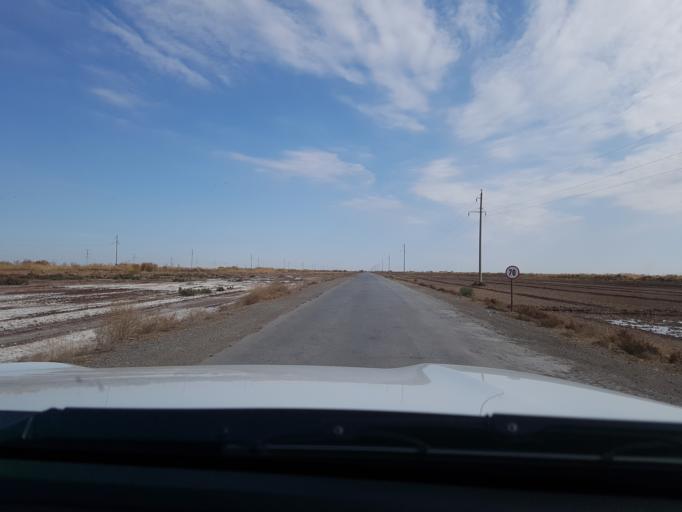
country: TM
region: Ahal
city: Tejen
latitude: 37.4466
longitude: 61.0940
